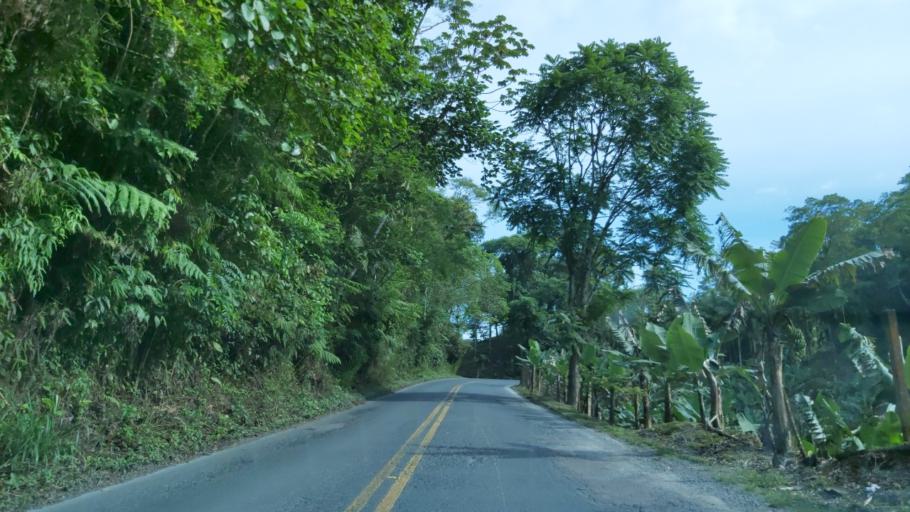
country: BR
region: Sao Paulo
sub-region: Juquia
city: Juquia
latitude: -24.0812
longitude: -47.6073
